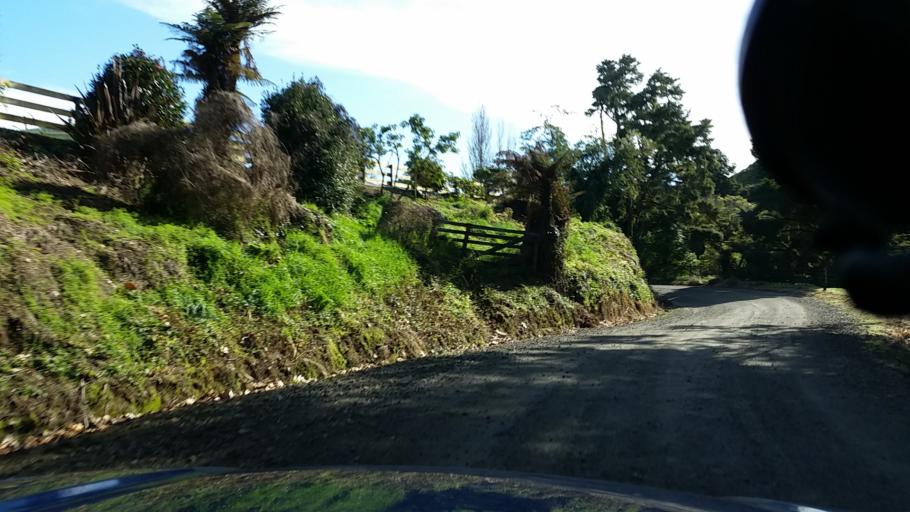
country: NZ
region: Taranaki
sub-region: New Plymouth District
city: Waitara
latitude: -39.0595
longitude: 174.7817
